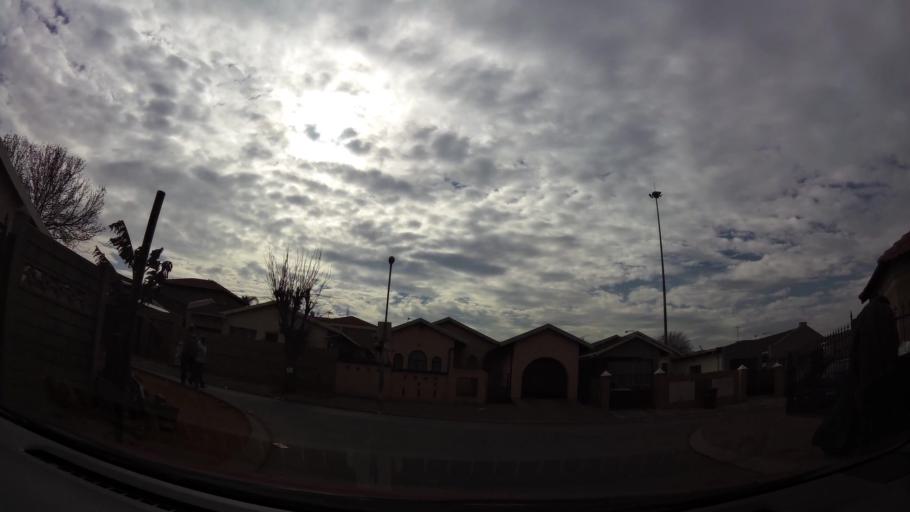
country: ZA
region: Gauteng
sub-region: City of Johannesburg Metropolitan Municipality
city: Soweto
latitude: -26.2733
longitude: 27.8324
